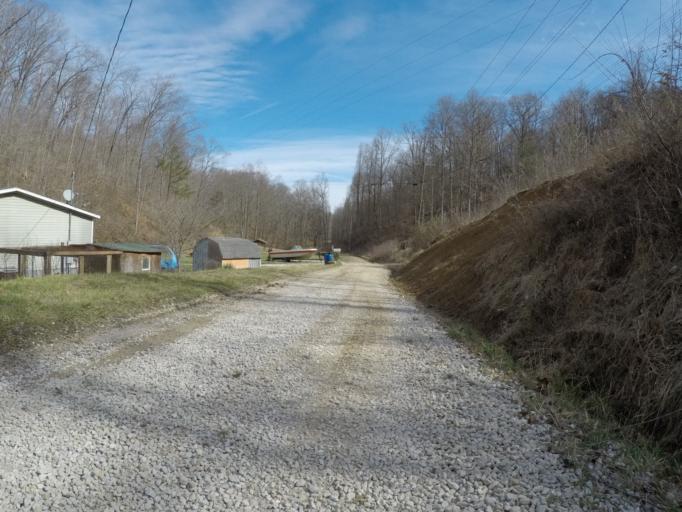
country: US
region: West Virginia
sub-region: Wayne County
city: Ceredo
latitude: 38.3451
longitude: -82.5477
